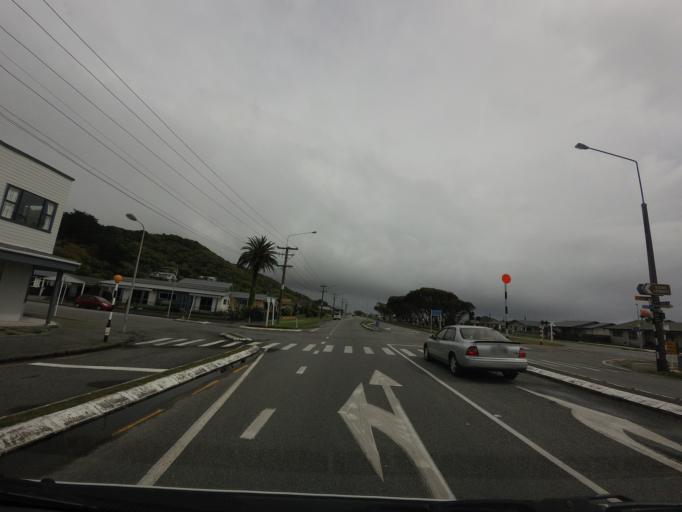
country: NZ
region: West Coast
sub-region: Grey District
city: Greymouth
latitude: -42.4663
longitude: 171.1921
